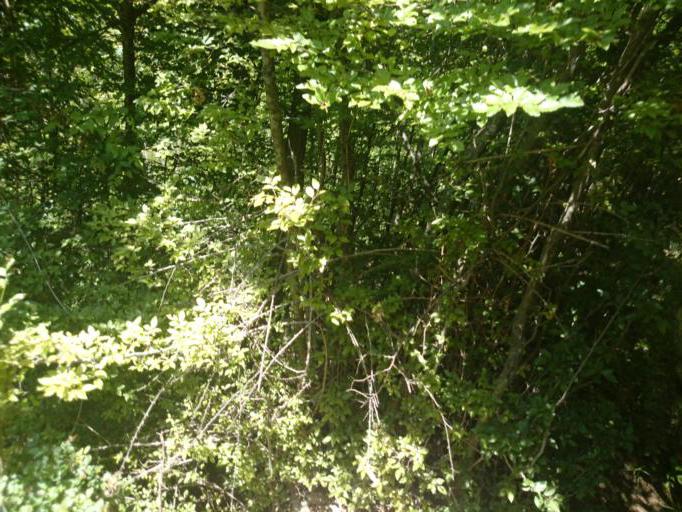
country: AL
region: Diber
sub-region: Rrethi i Dibres
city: Melan
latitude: 41.6183
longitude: 20.4218
